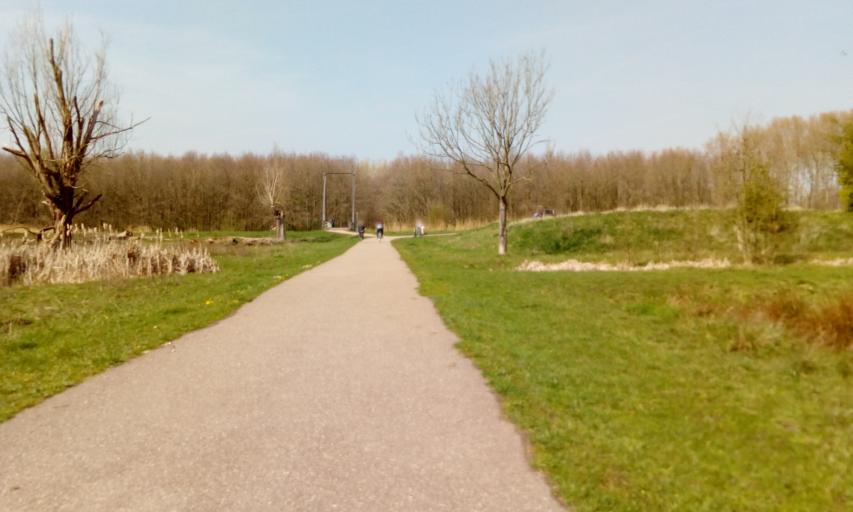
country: NL
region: South Holland
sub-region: Gemeente Spijkenisse
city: Spijkenisse
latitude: 51.8430
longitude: 4.3078
